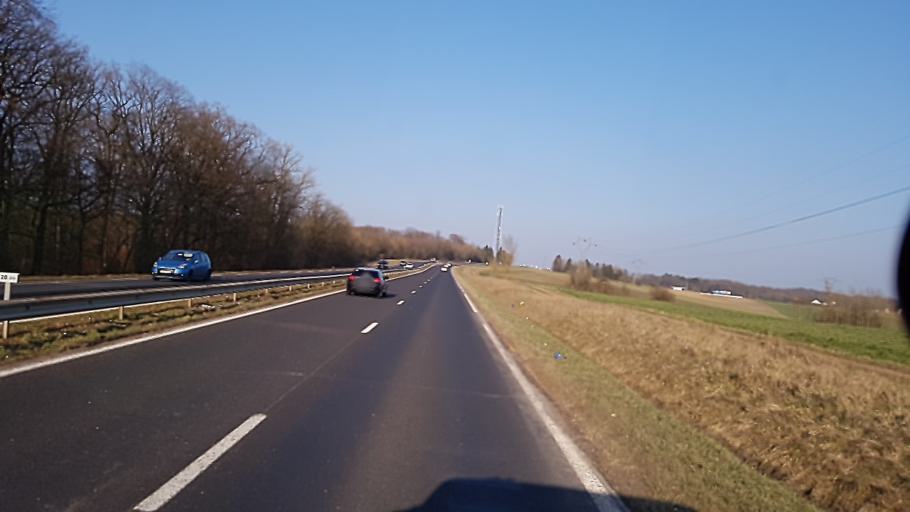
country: FR
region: Lorraine
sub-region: Departement de la Moselle
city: Woustviller
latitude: 49.0828
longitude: 7.0283
